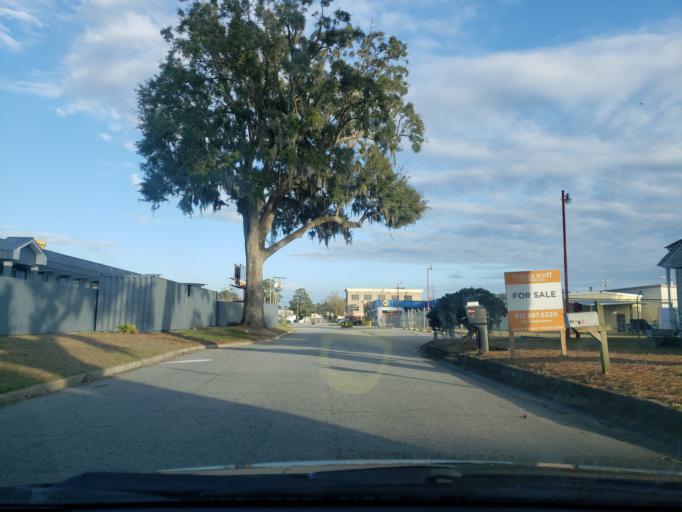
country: US
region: Georgia
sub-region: Chatham County
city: Isle of Hope
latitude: 32.0098
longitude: -81.1165
